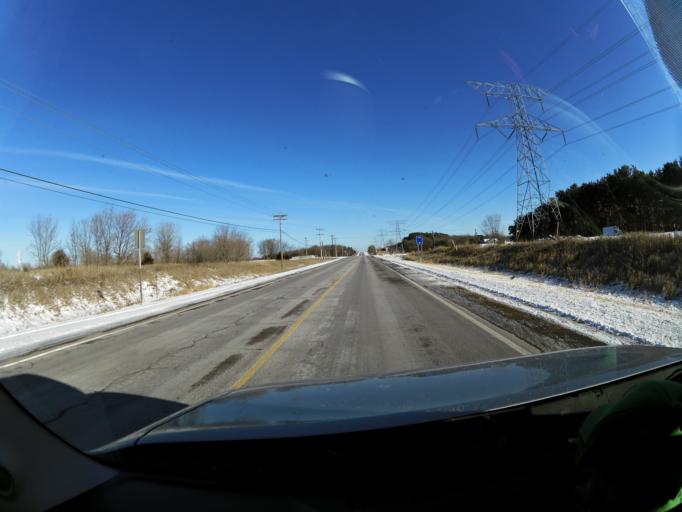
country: US
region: Minnesota
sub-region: Washington County
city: Lake Elmo
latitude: 44.9469
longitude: -92.8448
